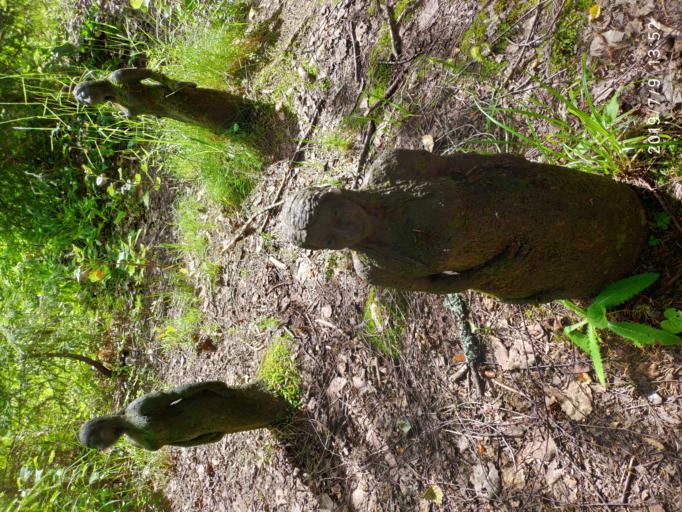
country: NO
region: Buskerud
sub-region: Sigdal
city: Prestfoss
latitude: 60.0611
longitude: 9.5049
